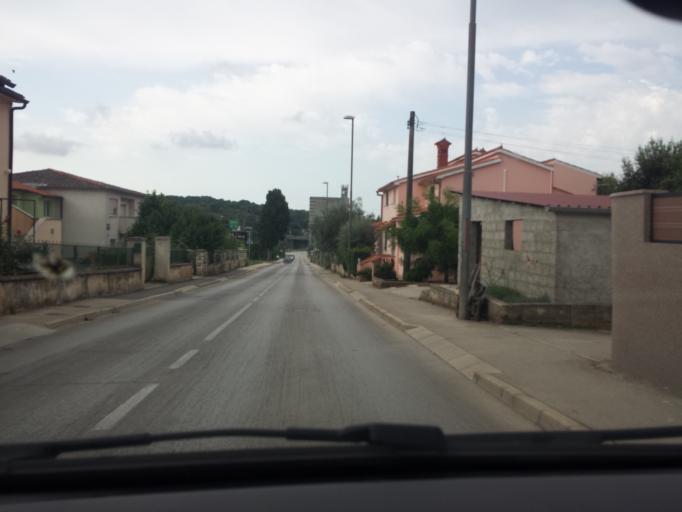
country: HR
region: Istarska
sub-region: Grad Pula
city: Pula
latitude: 44.8893
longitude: 13.8502
